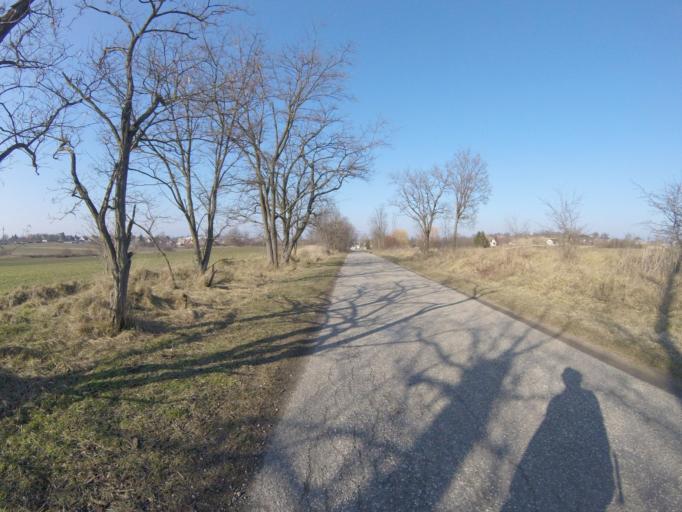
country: HU
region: Komarom-Esztergom
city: Oroszlany
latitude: 47.4774
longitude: 18.3307
